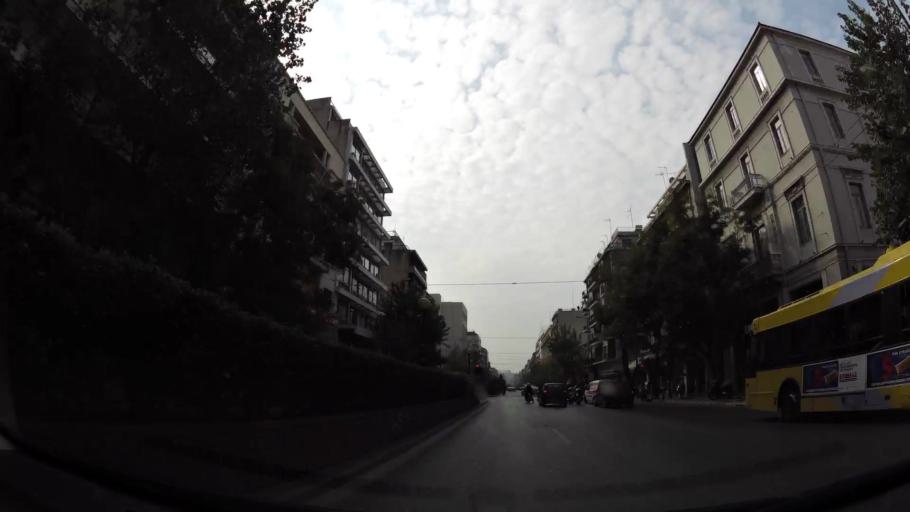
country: GR
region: Attica
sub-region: Nomarchia Athinas
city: Kipseli
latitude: 37.9952
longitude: 23.7322
